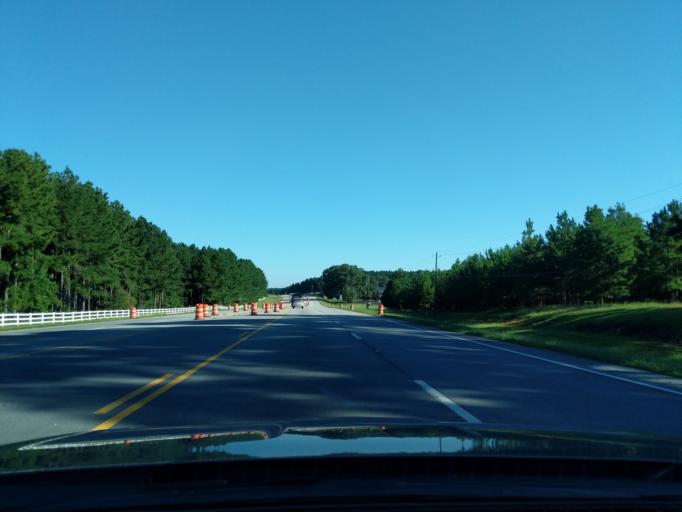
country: US
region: Georgia
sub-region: McDuffie County
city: Thomson
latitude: 33.5441
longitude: -82.5088
